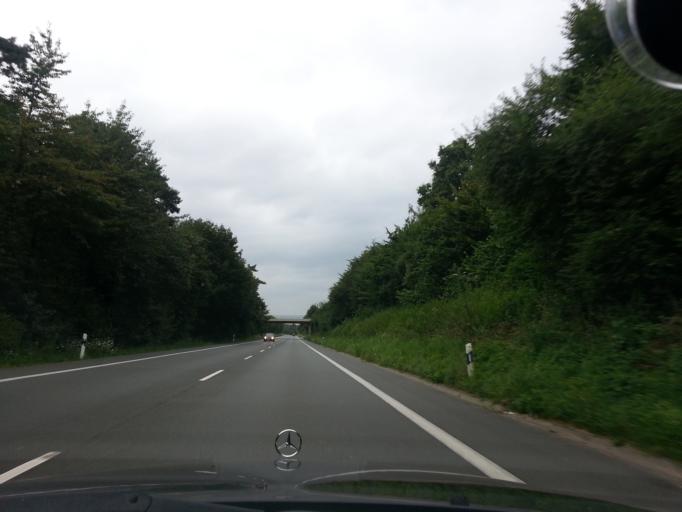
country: DE
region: North Rhine-Westphalia
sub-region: Regierungsbezirk Munster
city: Borken
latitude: 51.8499
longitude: 6.8359
